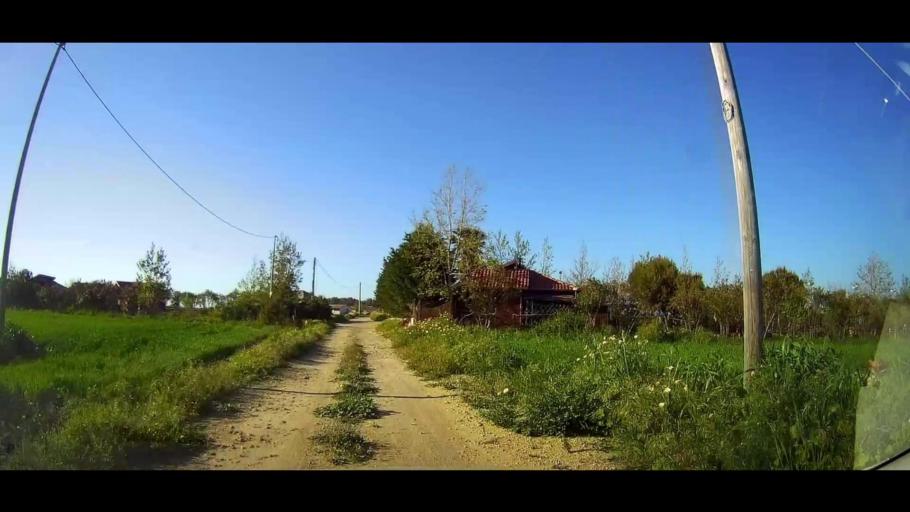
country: IT
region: Calabria
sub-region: Provincia di Crotone
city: Crotone
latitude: 39.0199
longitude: 17.1864
